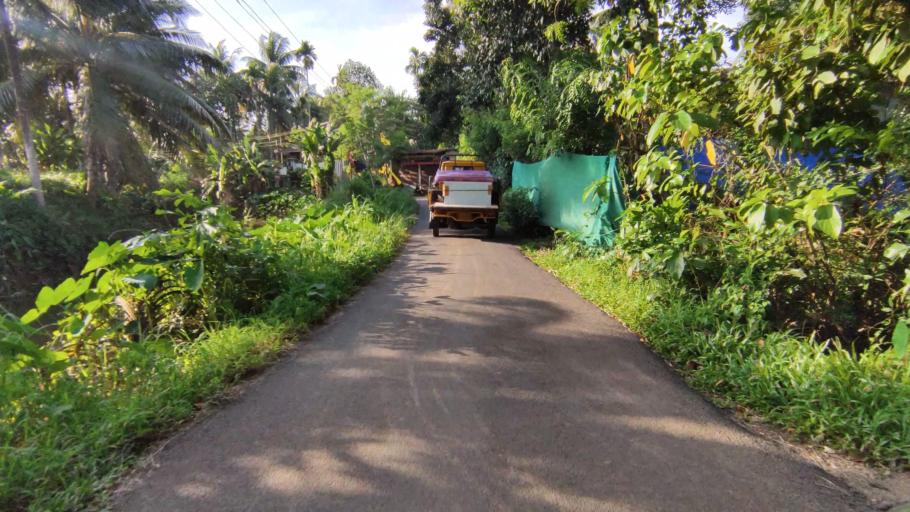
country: IN
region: Kerala
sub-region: Kottayam
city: Kottayam
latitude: 9.5966
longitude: 76.4874
